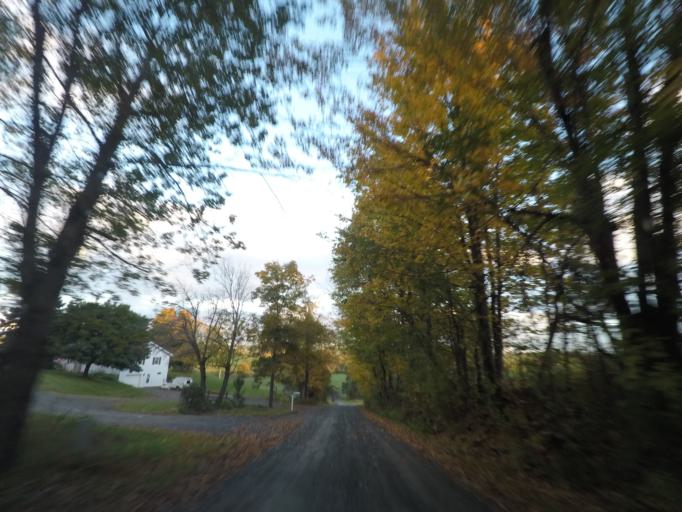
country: US
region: New York
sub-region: Rensselaer County
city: Nassau
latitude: 42.4918
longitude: -73.5882
